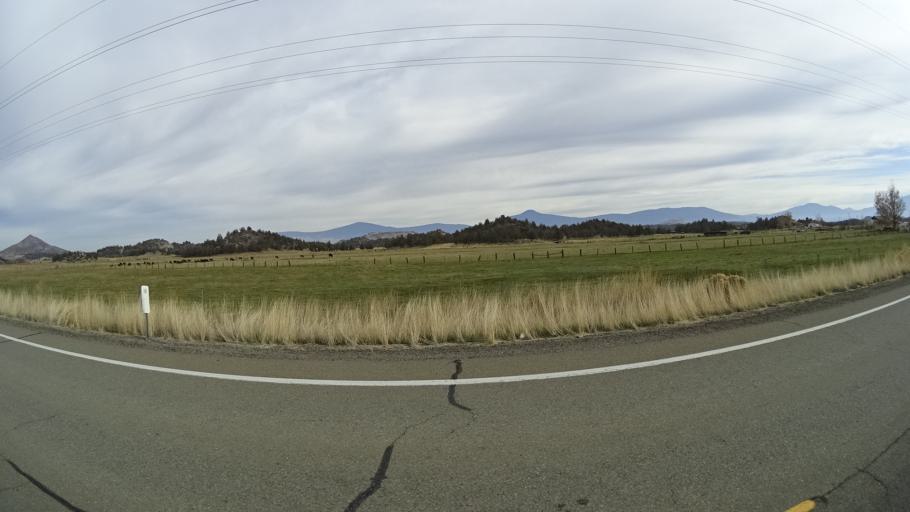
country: US
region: California
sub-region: Siskiyou County
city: Montague
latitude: 41.6745
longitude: -122.5255
